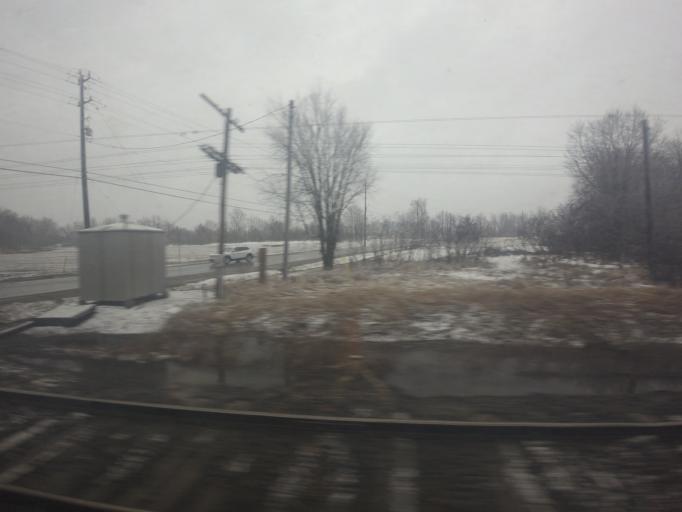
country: US
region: New York
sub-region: Jefferson County
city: Alexandria Bay
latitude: 44.4914
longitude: -75.8725
